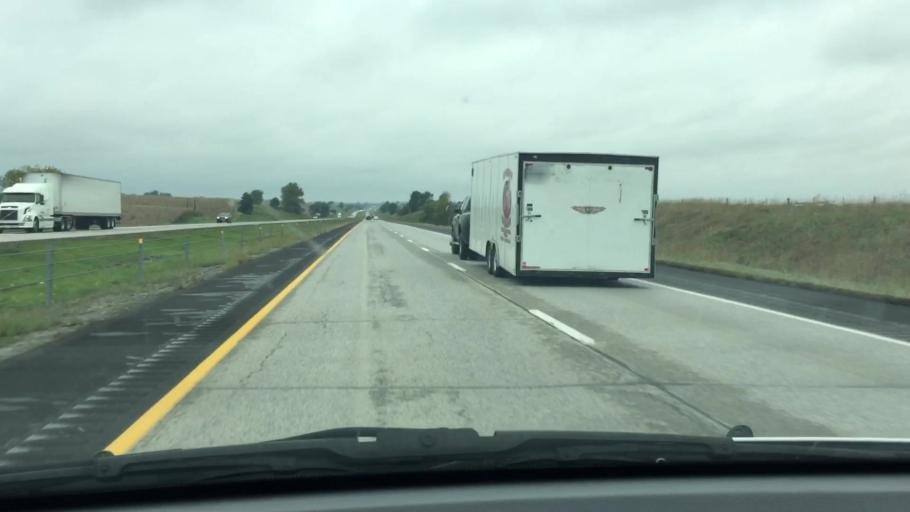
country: US
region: Iowa
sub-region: Iowa County
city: Williamsburg
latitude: 41.6873
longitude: -91.8603
